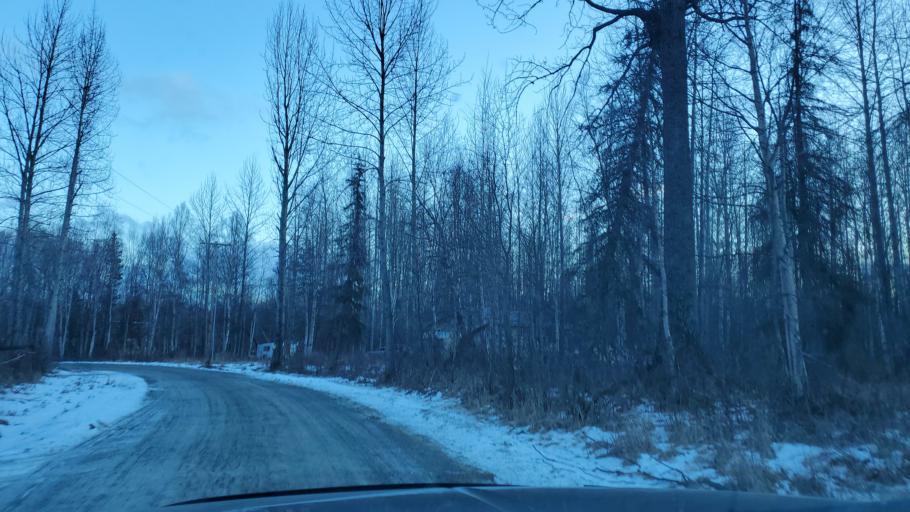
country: US
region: Alaska
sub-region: Matanuska-Susitna Borough
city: Lakes
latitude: 61.6654
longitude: -149.3387
